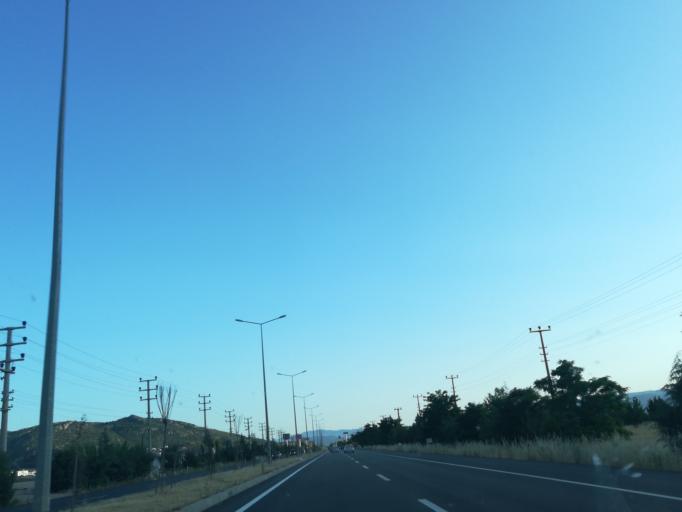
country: TR
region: Burdur
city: Bucak
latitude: 37.4148
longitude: 30.5459
